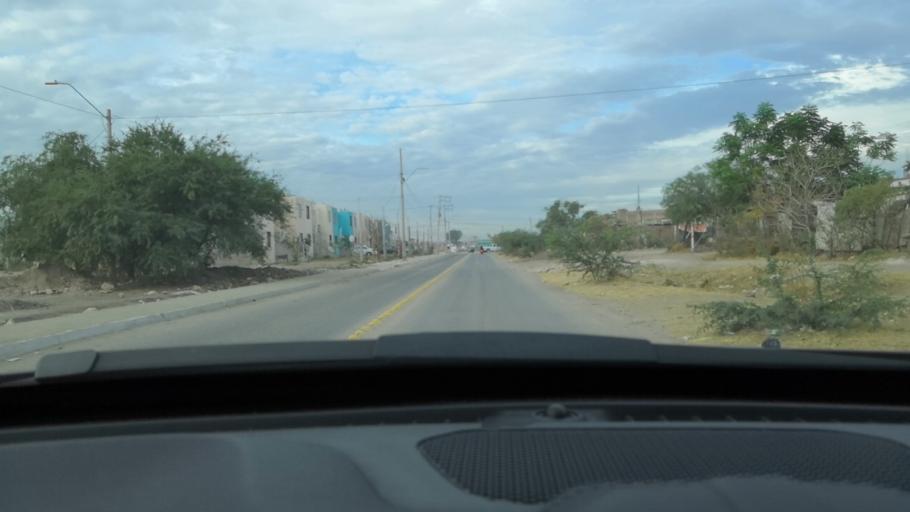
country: MX
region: Guanajuato
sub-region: Leon
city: Fraccionamiento Paraiso Real
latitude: 21.0929
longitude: -101.5960
